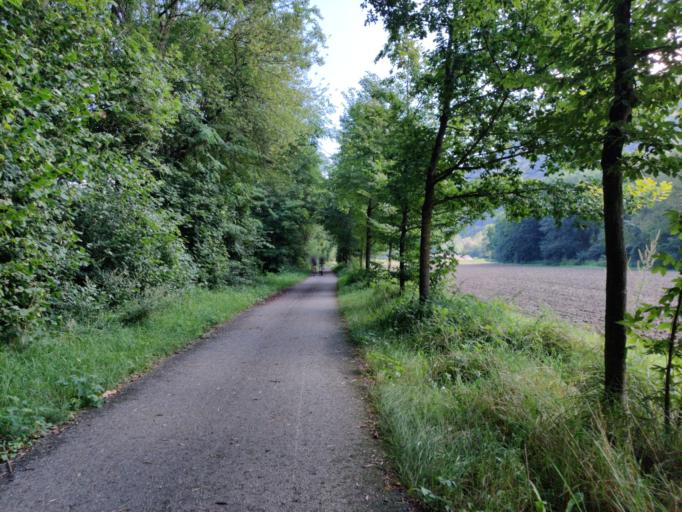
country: AT
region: Lower Austria
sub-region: Politischer Bezirk Krems
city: Aggsbach
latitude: 48.2783
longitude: 15.3967
